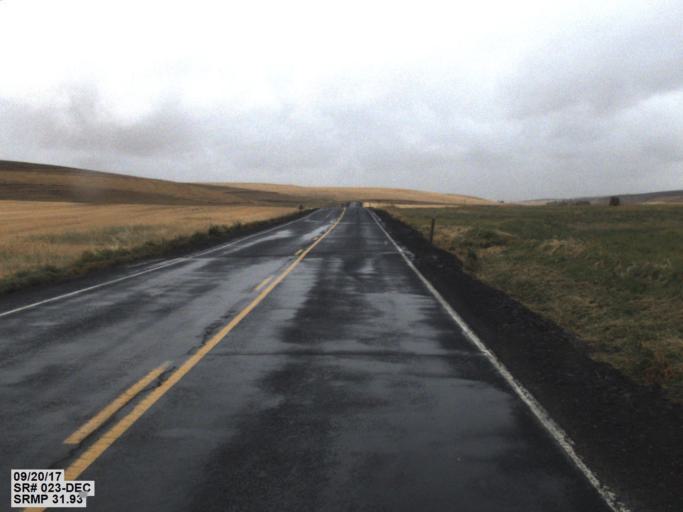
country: US
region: Washington
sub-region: Spokane County
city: Cheney
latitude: 47.1662
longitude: -117.8703
